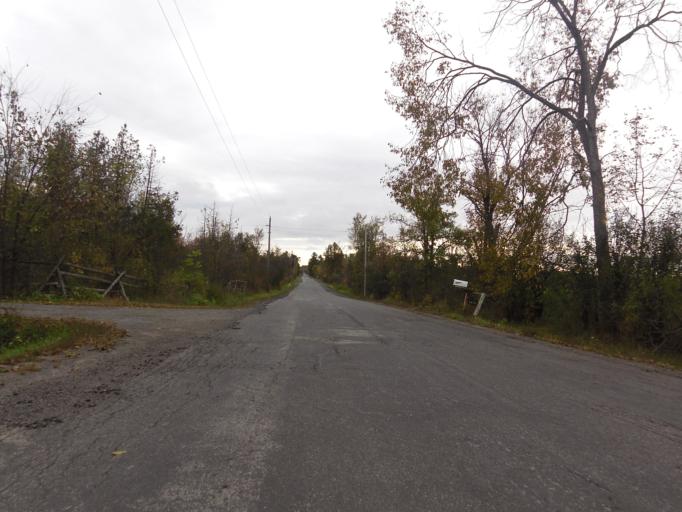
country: CA
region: Ontario
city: Arnprior
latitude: 45.4615
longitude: -76.1449
